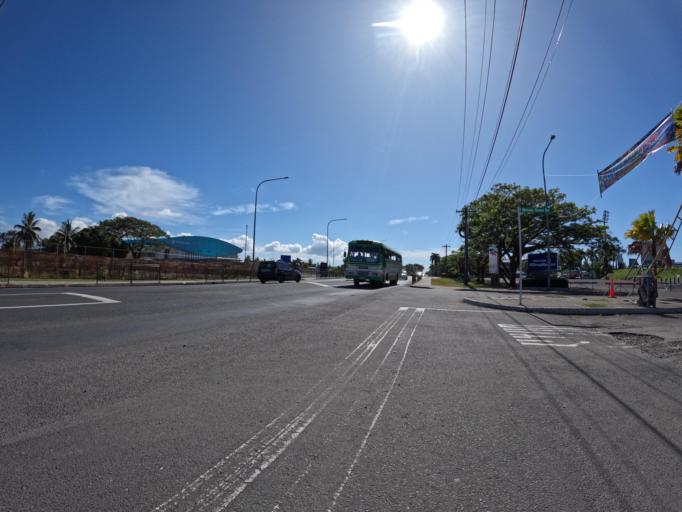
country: FJ
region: Central
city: Suva
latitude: -18.1483
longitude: 178.4485
